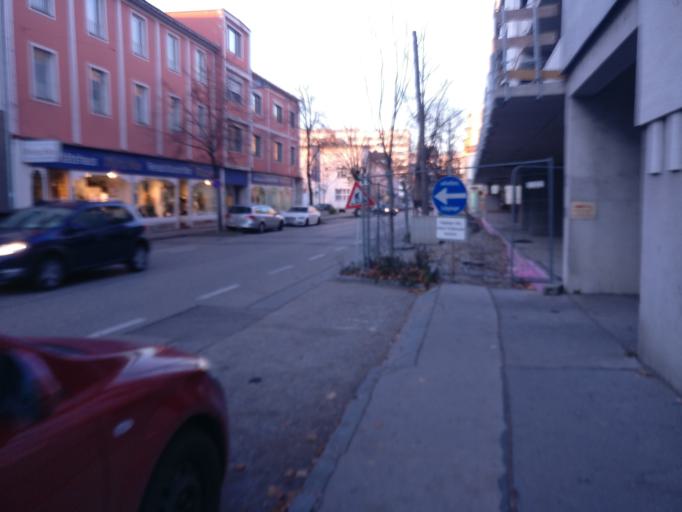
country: AT
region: Lower Austria
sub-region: Sankt Polten Stadt
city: Sankt Poelten
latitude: 48.2112
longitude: 15.6250
